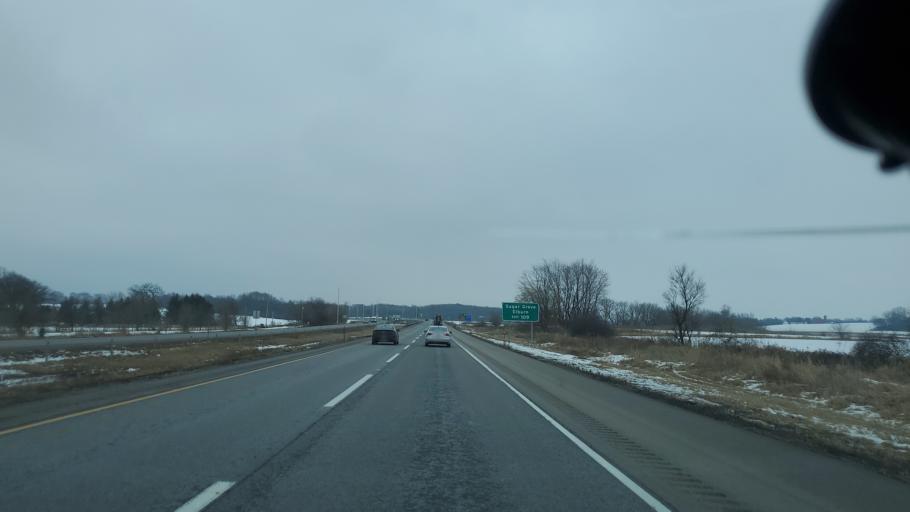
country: US
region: Illinois
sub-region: Kane County
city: Elburn
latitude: 41.8254
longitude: -88.4775
